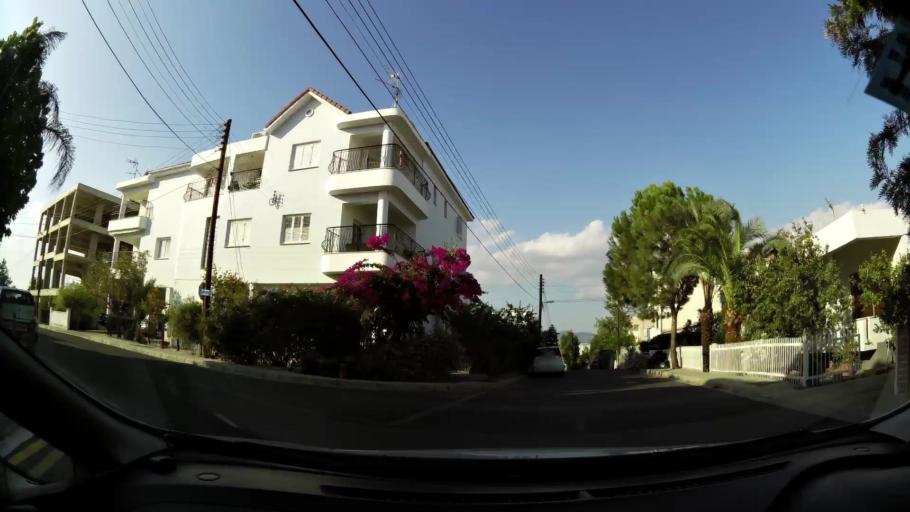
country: CY
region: Lefkosia
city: Nicosia
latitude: 35.1724
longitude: 33.3322
